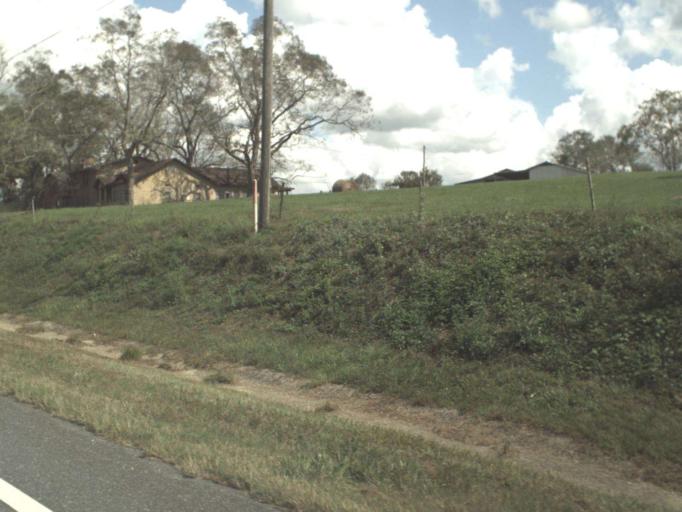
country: US
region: Florida
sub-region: Washington County
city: Chipley
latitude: 30.8082
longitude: -85.5127
